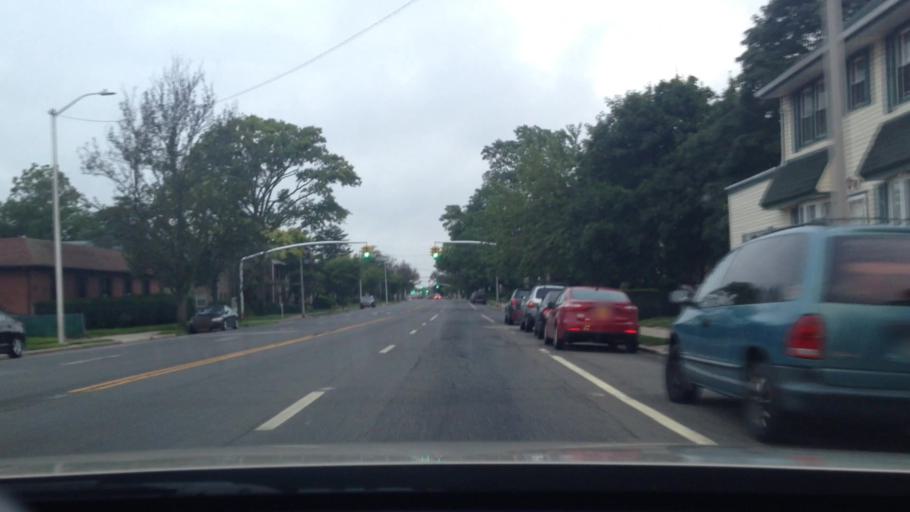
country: US
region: New York
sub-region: Nassau County
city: Rockville Centre
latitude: 40.6552
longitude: -73.6371
